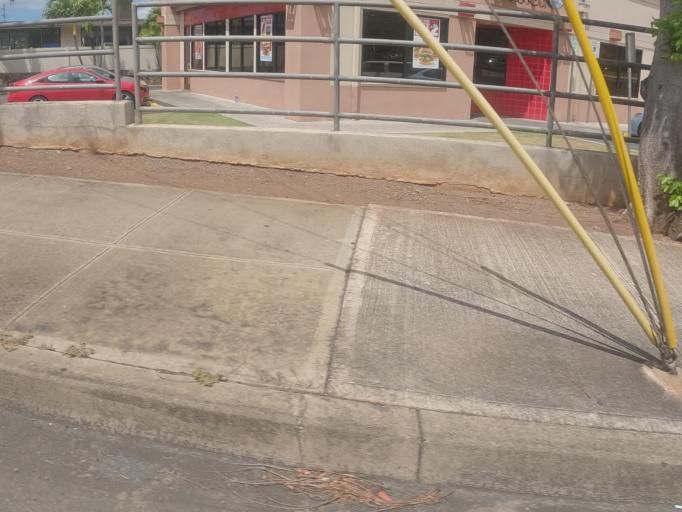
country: US
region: Hawaii
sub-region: Honolulu County
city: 'Aiea
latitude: 21.3776
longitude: -157.9310
